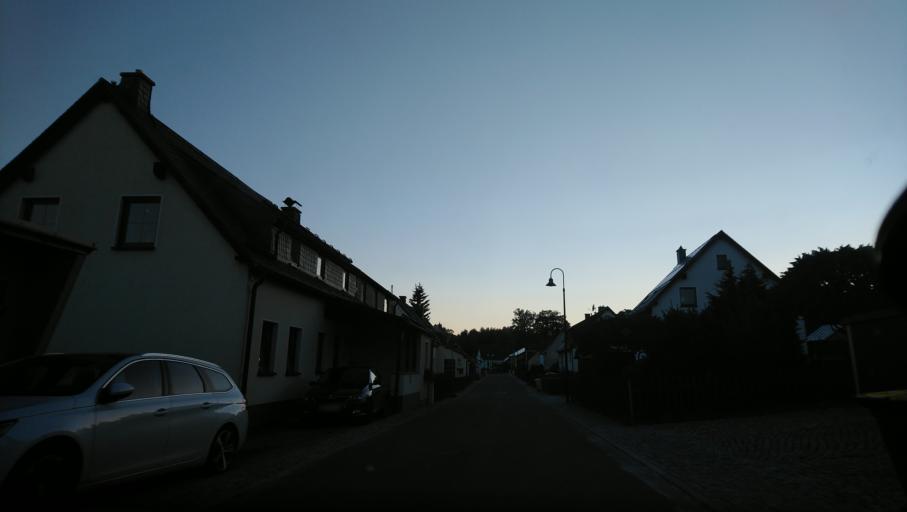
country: CZ
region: Ustecky
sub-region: Okres Chomutov
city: Vejprty
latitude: 50.4932
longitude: 13.0212
